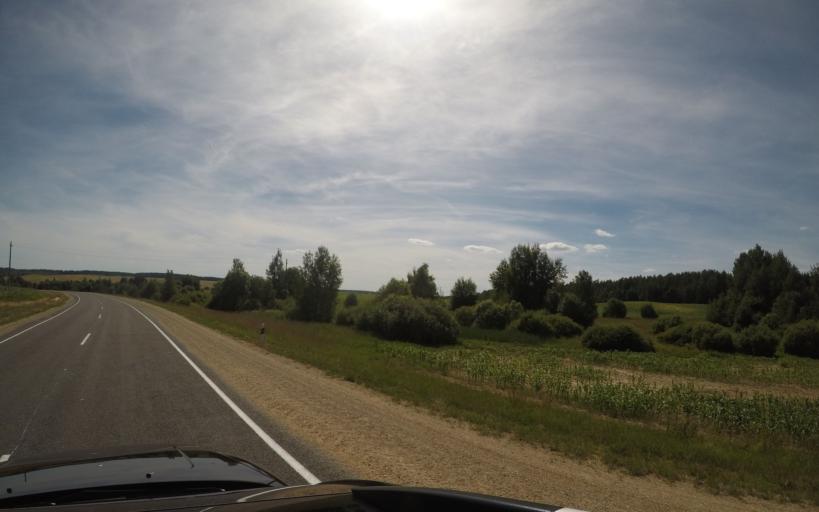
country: BY
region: Grodnenskaya
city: Hal'shany
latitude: 54.2654
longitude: 25.9879
